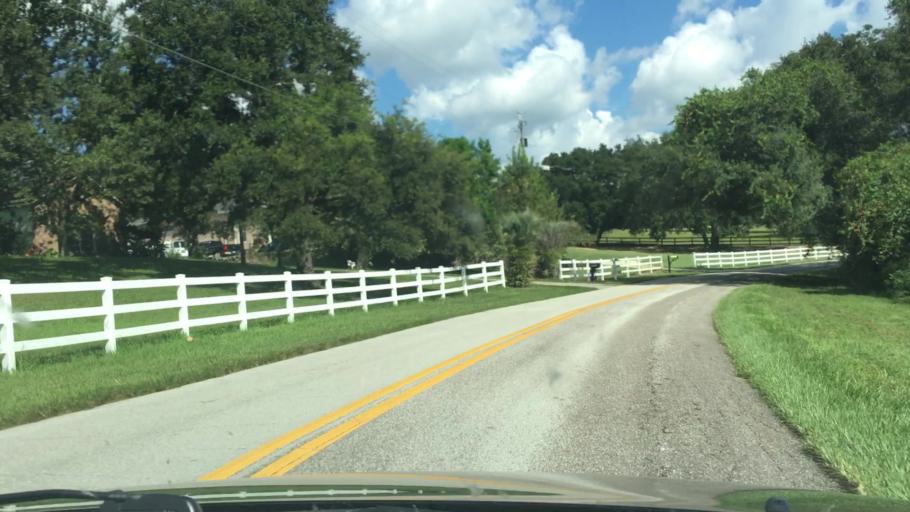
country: US
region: Florida
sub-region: Lake County
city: Montverde
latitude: 28.5927
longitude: -81.6911
